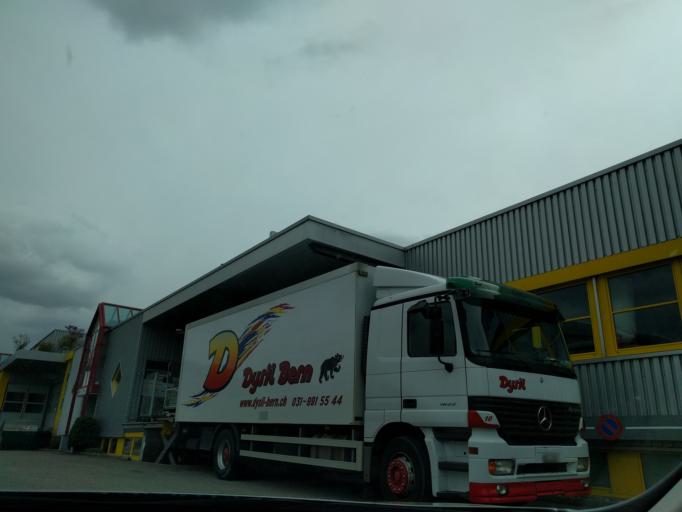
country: CH
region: Fribourg
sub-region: Sense District
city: Schmitten
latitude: 46.8633
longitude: 7.2484
